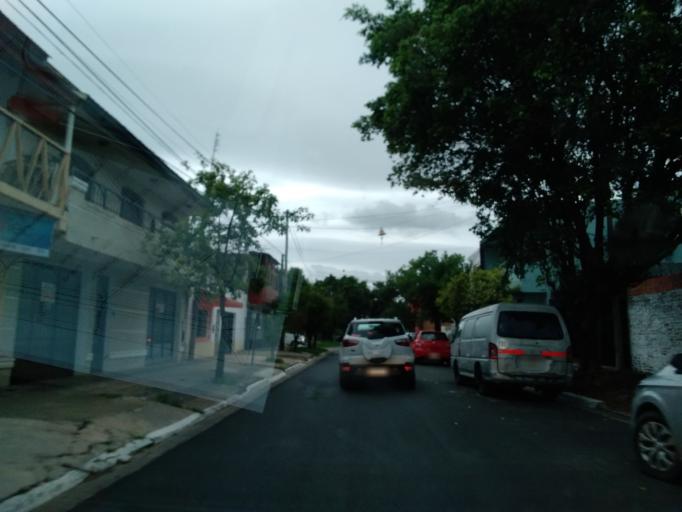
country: AR
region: Corrientes
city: Corrientes
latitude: -27.4751
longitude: -58.8248
